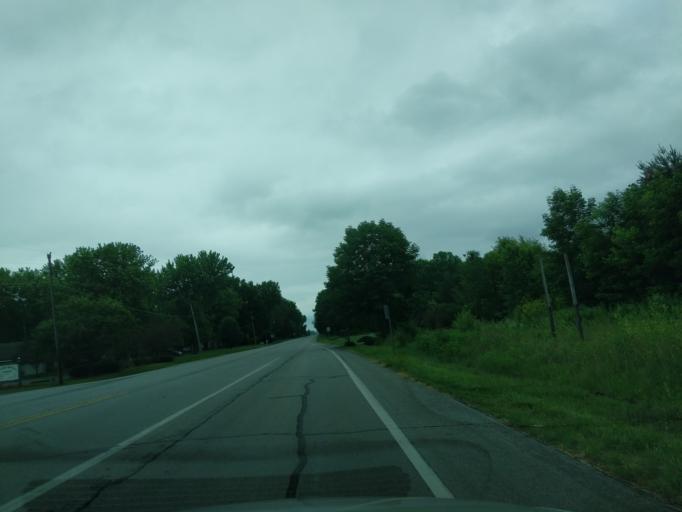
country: US
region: Indiana
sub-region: Hamilton County
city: Noblesville
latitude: 40.0726
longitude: -86.0146
